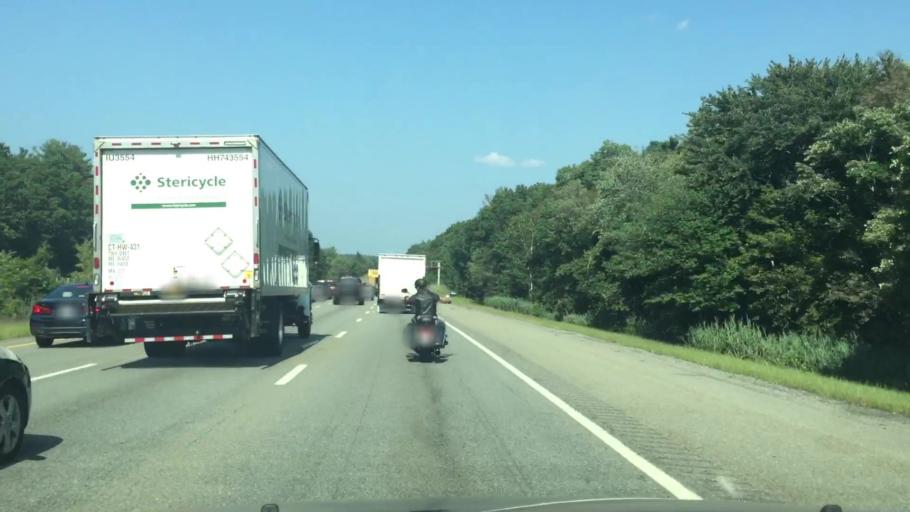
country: US
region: Massachusetts
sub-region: Middlesex County
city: Westford
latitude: 42.5603
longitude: -71.4364
